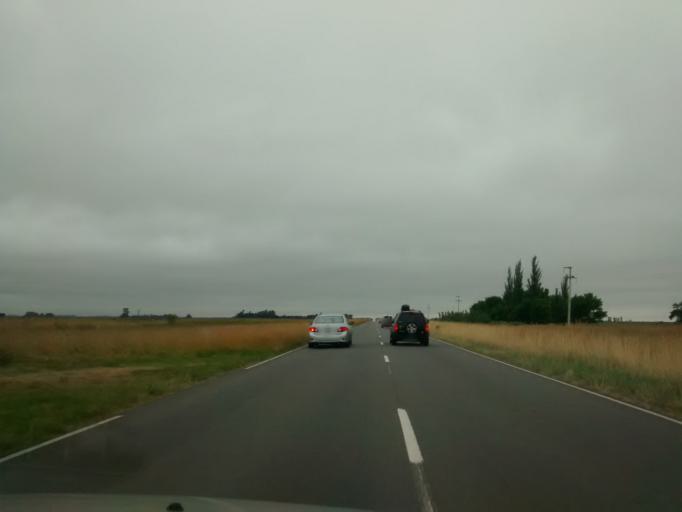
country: AR
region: Buenos Aires
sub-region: Partido de Ayacucho
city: Ayacucho
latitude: -37.0285
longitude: -58.5395
